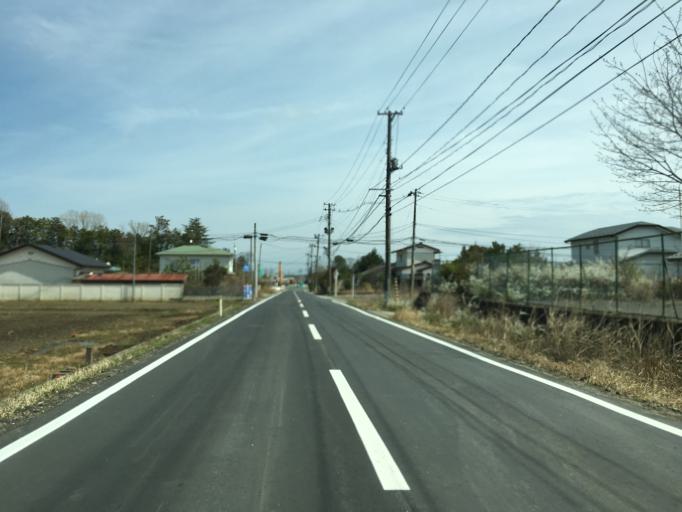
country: JP
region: Fukushima
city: Namie
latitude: 37.4559
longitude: 141.0020
